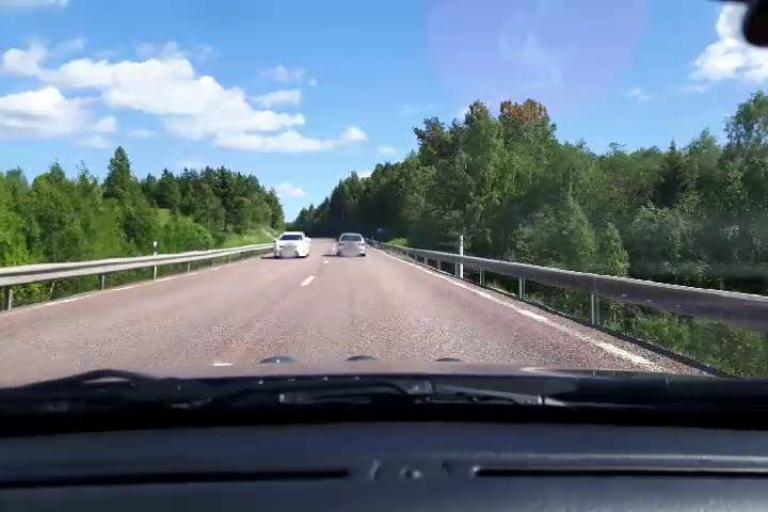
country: SE
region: Gaevleborg
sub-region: Hudiksvalls Kommun
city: Sorforsa
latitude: 61.7418
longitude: 16.8599
